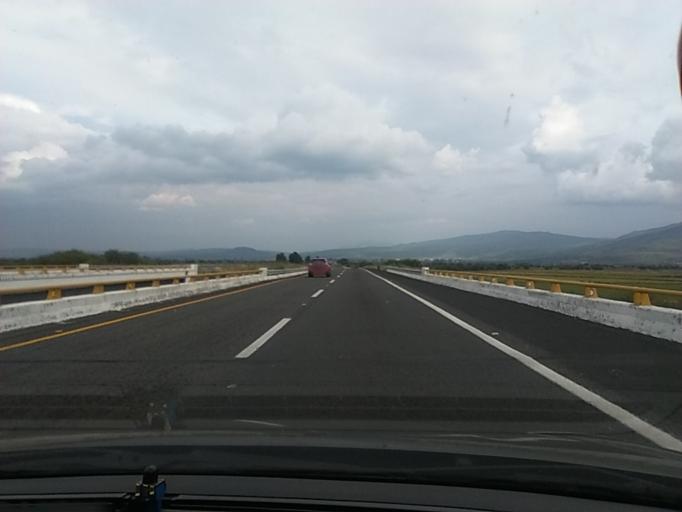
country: MX
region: Michoacan
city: Ecuandureo
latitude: 20.1788
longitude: -102.2650
